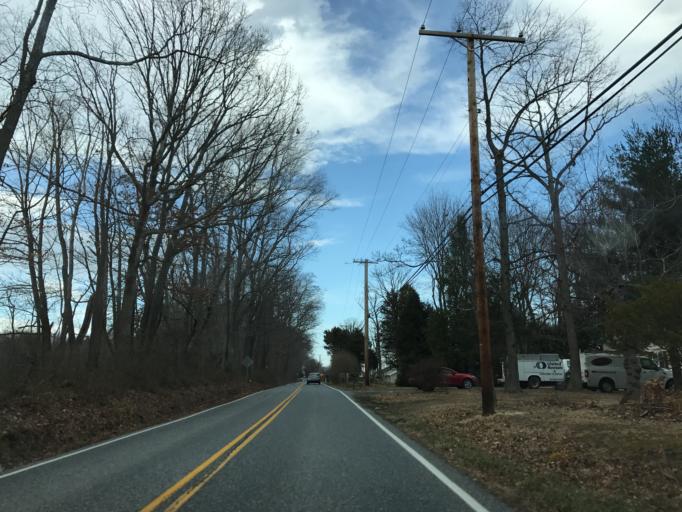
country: US
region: Maryland
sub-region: Harford County
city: Bel Air South
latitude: 39.5283
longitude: -76.2827
